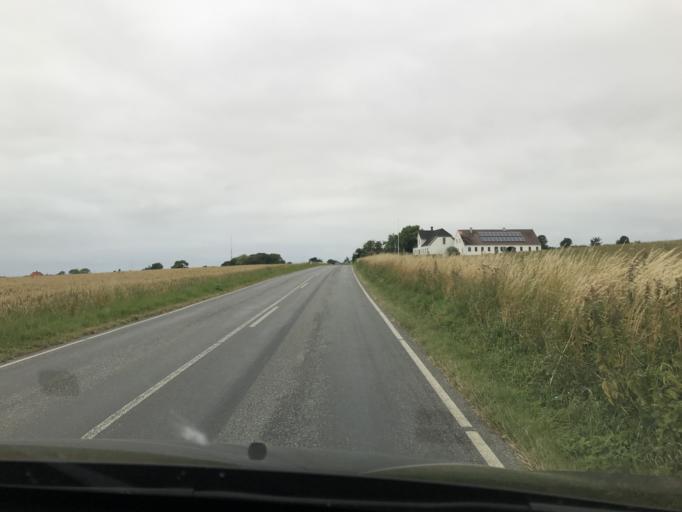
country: DK
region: South Denmark
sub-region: AEro Kommune
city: AEroskobing
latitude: 54.8462
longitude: 10.4261
